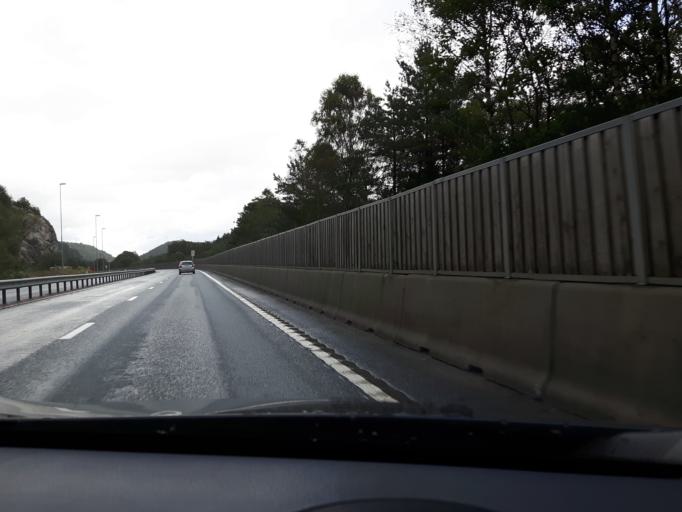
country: NO
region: Vest-Agder
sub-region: Sogne
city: Tangvall
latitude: 58.1138
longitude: 7.8355
